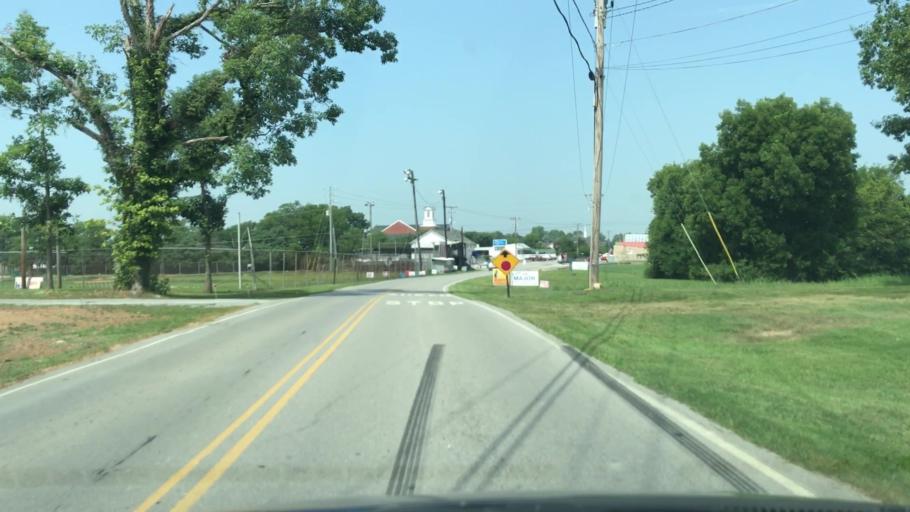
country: US
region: Tennessee
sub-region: Wilson County
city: Rural Hill
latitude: 36.1129
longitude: -86.4135
